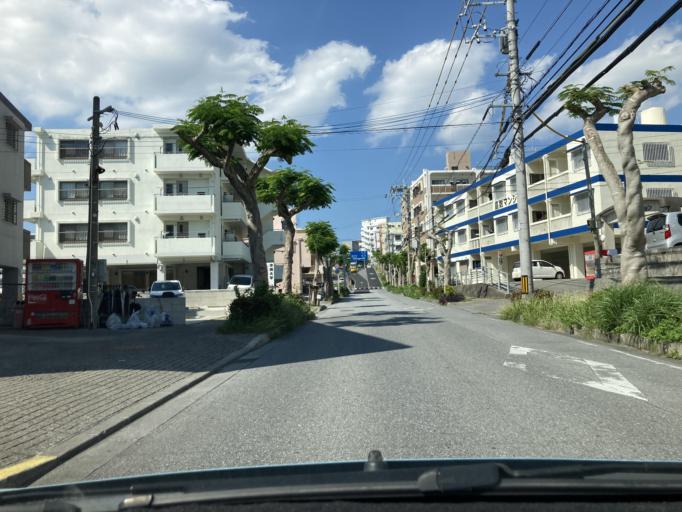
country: JP
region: Okinawa
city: Tomigusuku
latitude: 26.1983
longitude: 127.6994
